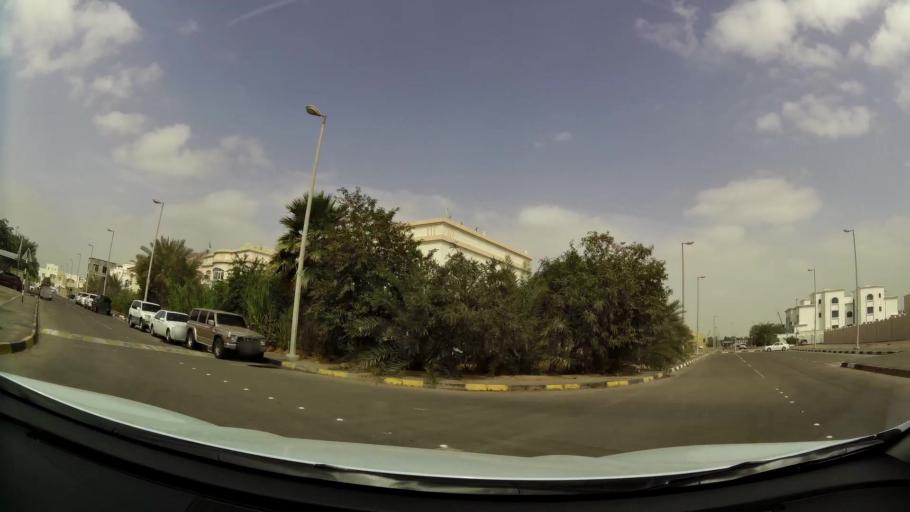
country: AE
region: Abu Dhabi
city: Abu Dhabi
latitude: 24.3946
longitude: 54.4964
